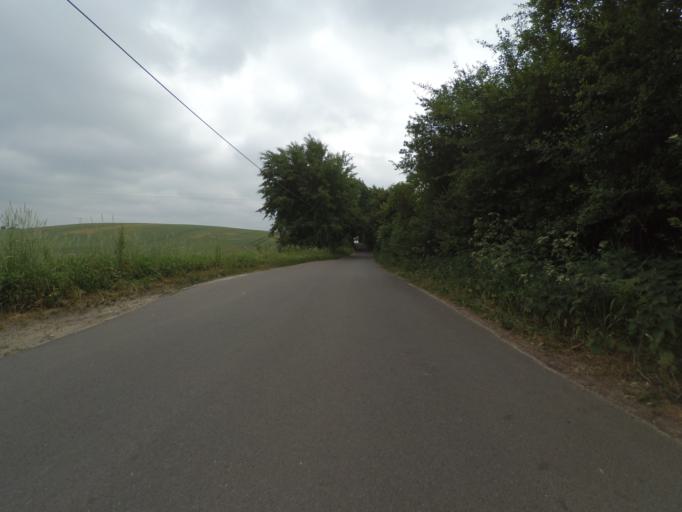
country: DE
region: Mecklenburg-Vorpommern
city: Krakow am See
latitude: 53.6680
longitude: 12.3127
